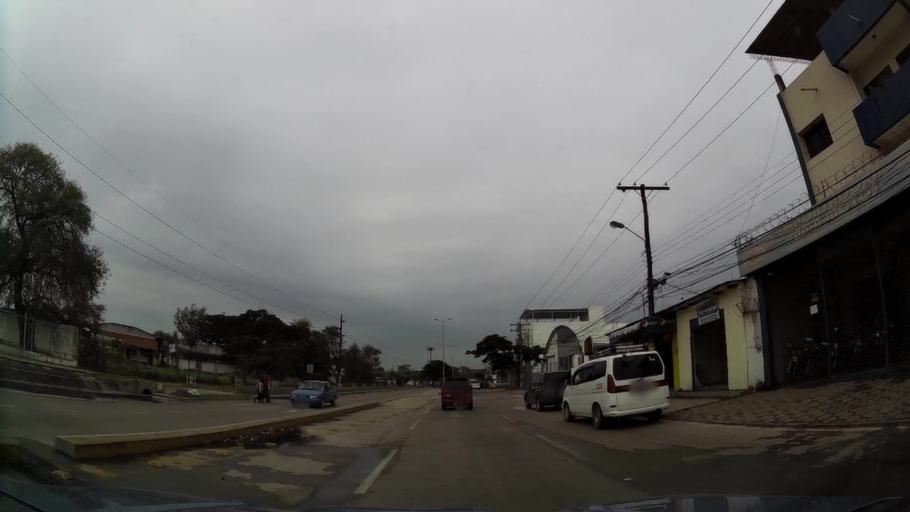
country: BO
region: Santa Cruz
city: Santa Cruz de la Sierra
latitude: -17.7684
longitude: -63.1574
